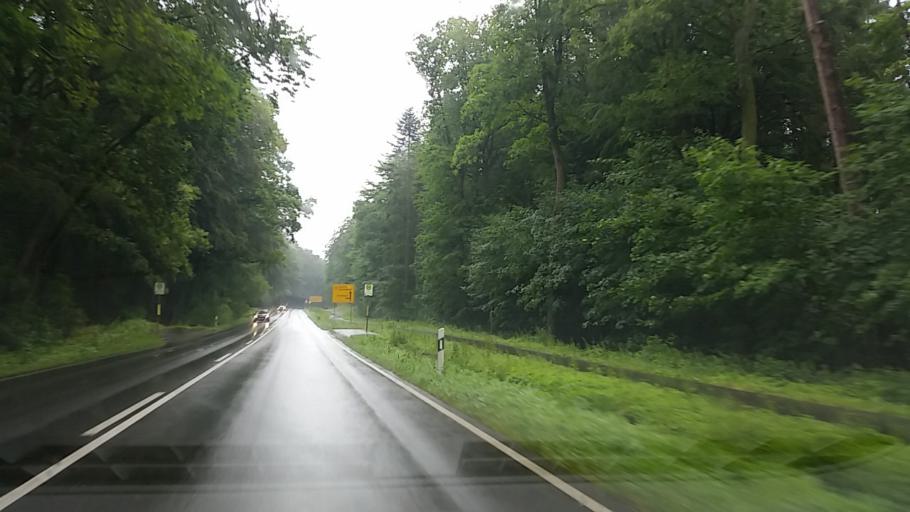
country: DE
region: Mecklenburg-Vorpommern
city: Bad Doberan
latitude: 54.0958
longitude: 11.8700
